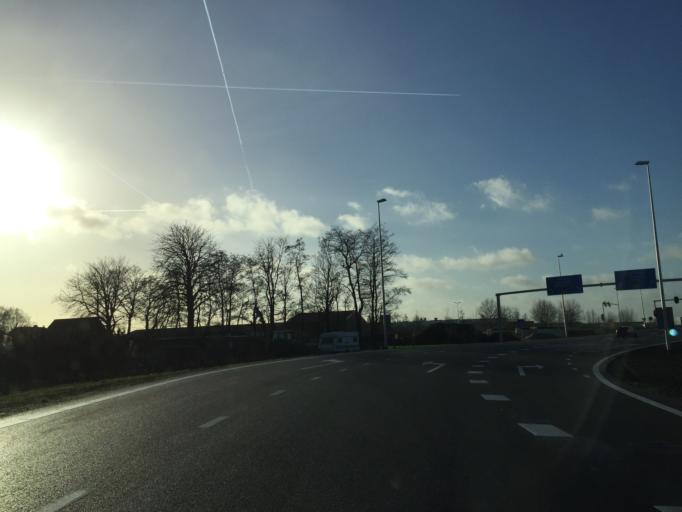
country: NL
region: South Holland
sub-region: Gemeente Waddinxveen
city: Waddinxveen
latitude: 52.0193
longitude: 4.6461
